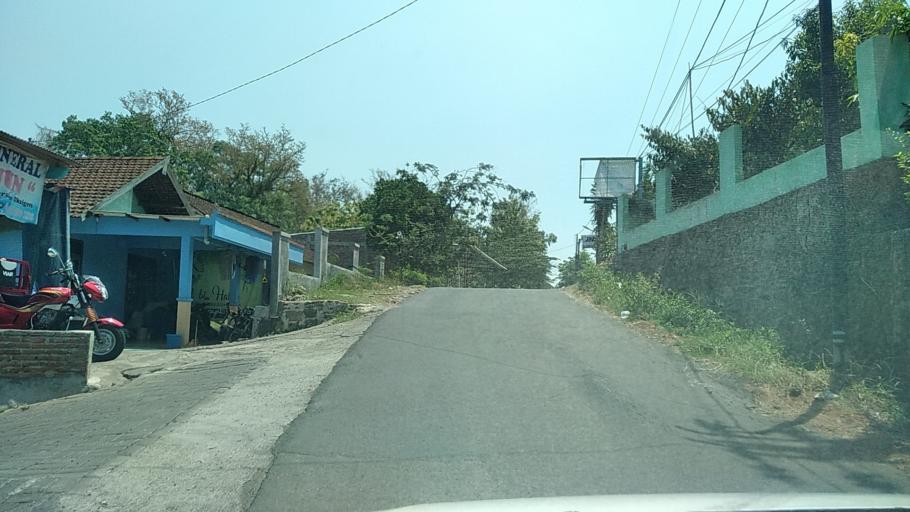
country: ID
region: Central Java
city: Semarang
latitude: -7.0206
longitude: 110.3834
